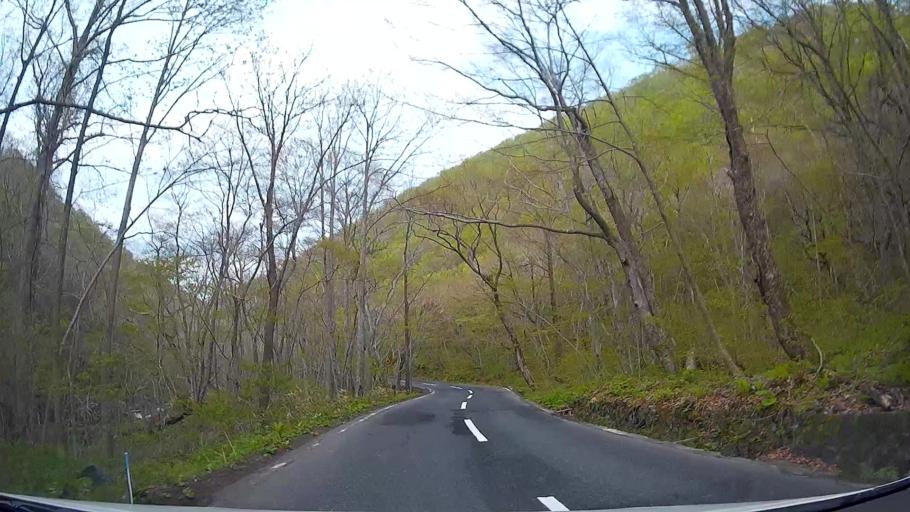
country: JP
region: Akita
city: Hanawa
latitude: 40.4804
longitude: 140.9442
